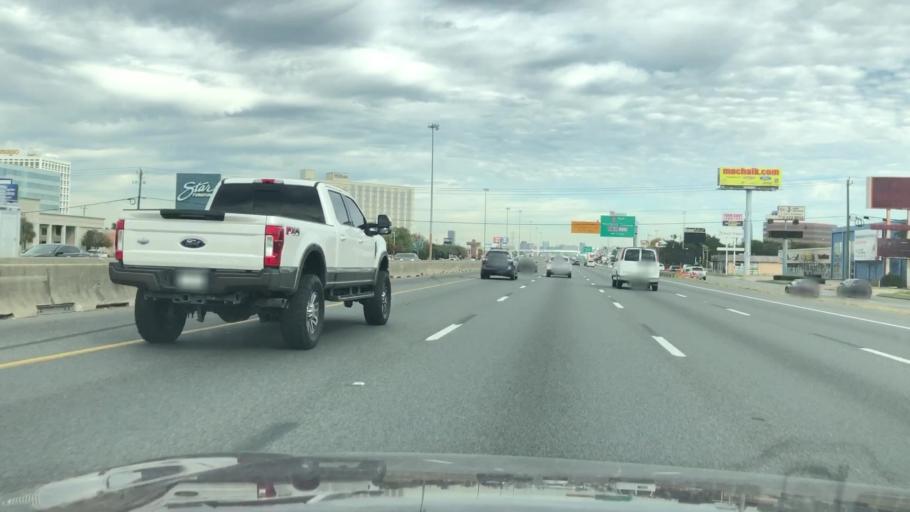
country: US
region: Texas
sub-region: Harris County
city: Bellaire
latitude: 29.7115
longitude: -95.5049
